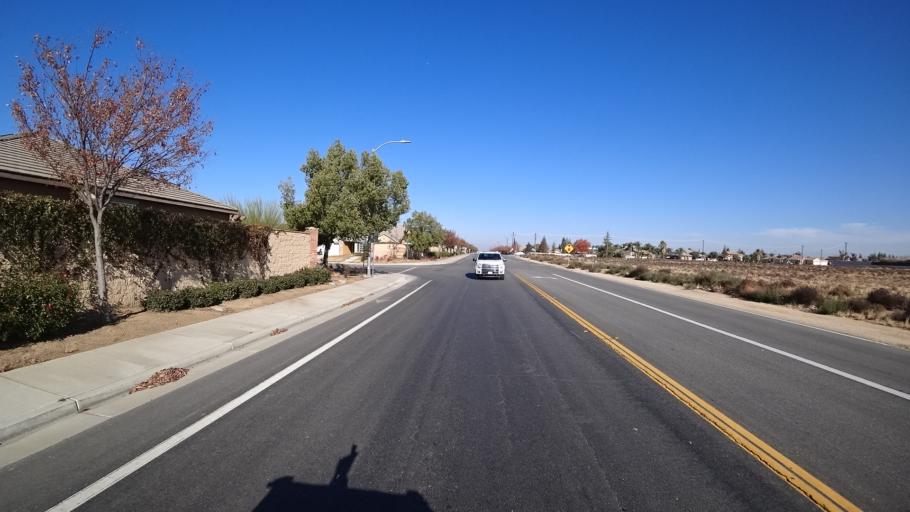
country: US
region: California
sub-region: Kern County
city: Rosedale
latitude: 35.4107
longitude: -119.1456
